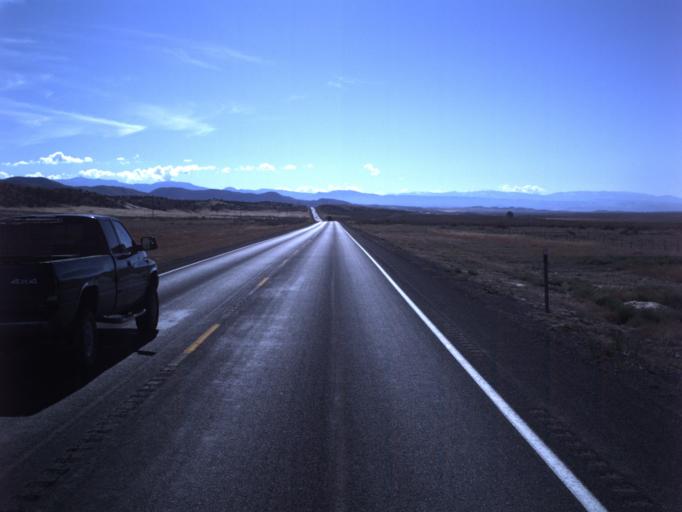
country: US
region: Utah
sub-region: Sanpete County
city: Gunnison
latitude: 39.3011
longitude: -111.8939
